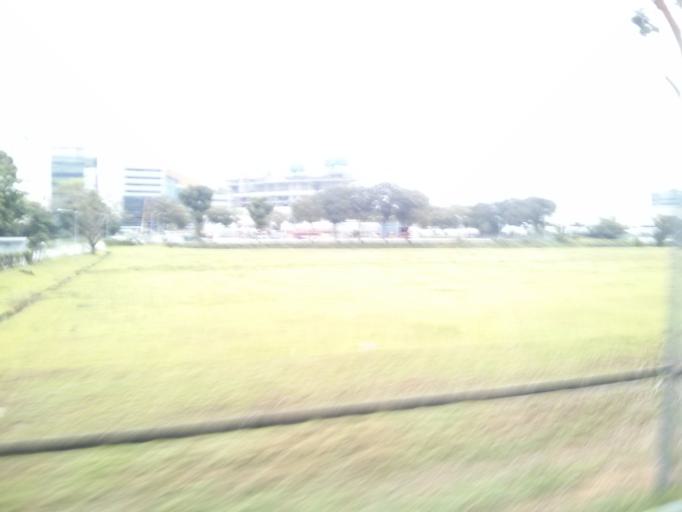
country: SG
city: Singapore
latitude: 1.2925
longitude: 103.7883
